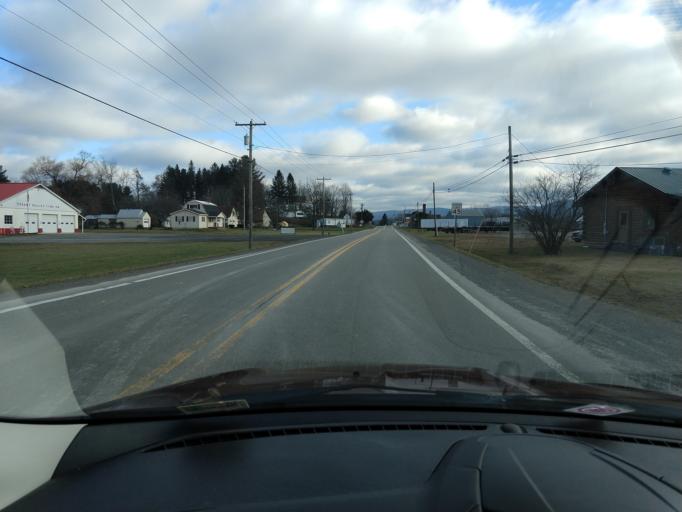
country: US
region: West Virginia
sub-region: Randolph County
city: Elkins
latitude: 38.7943
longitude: -79.9017
